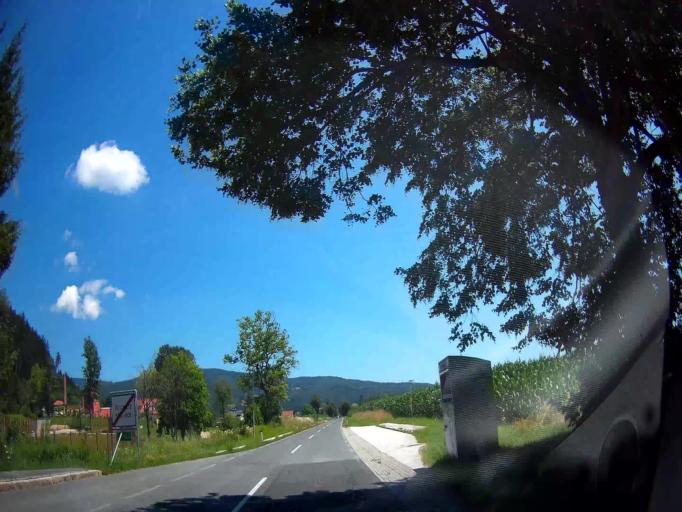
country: AT
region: Carinthia
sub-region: Politischer Bezirk Volkermarkt
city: Bleiburg/Pliberk
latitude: 46.5773
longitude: 14.7835
